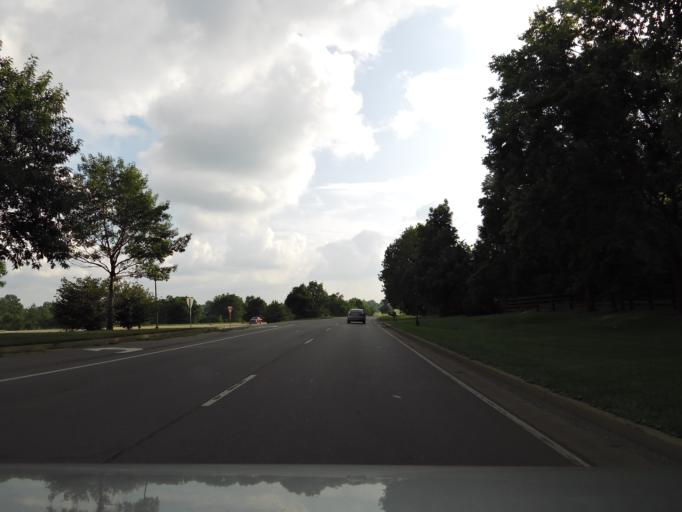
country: US
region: Kentucky
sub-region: Bourbon County
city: Paris
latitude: 38.1859
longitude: -84.2891
